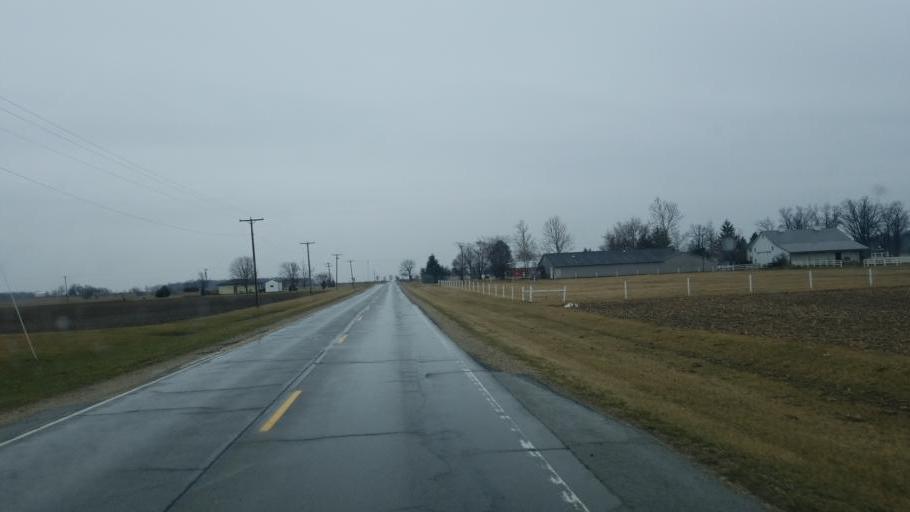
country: US
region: Indiana
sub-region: Adams County
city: Geneva
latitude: 40.6147
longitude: -85.0410
